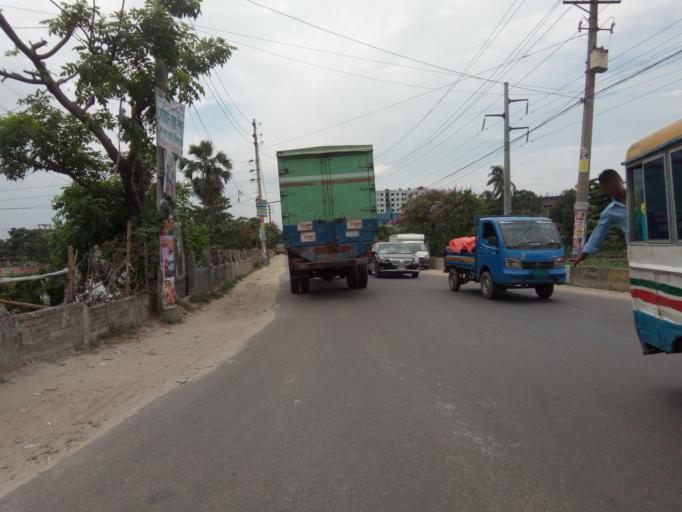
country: BD
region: Dhaka
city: Paltan
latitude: 23.7203
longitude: 90.4930
